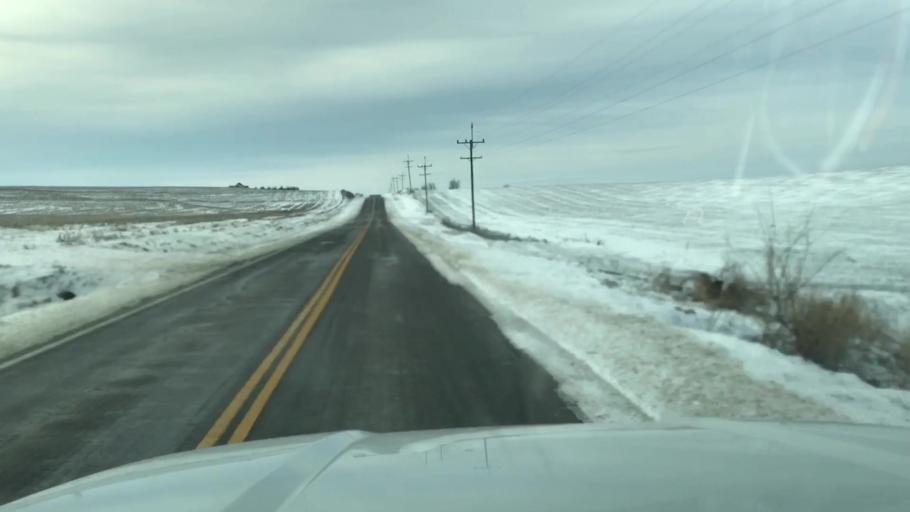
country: US
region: Missouri
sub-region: Holt County
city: Mound City
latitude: 40.1086
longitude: -95.1449
